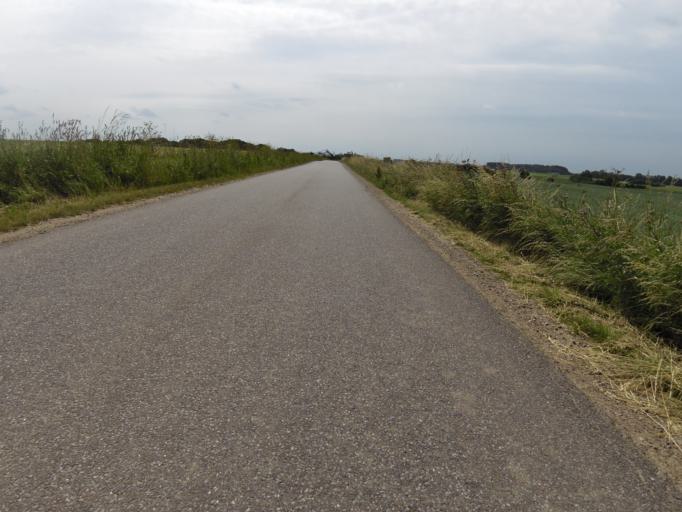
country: DK
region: Central Jutland
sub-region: Holstebro Kommune
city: Holstebro
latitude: 56.4308
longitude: 8.6374
